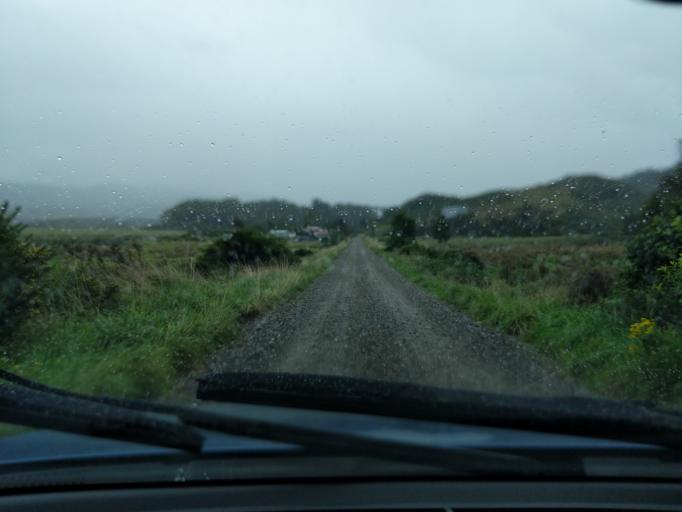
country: NZ
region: Tasman
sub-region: Tasman District
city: Takaka
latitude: -40.6338
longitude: 172.4900
